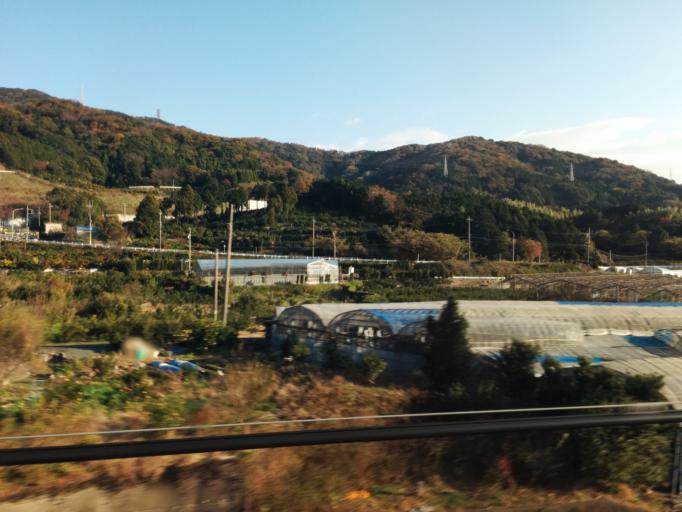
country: JP
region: Aichi
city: Gamagori
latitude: 34.8435
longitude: 137.2037
